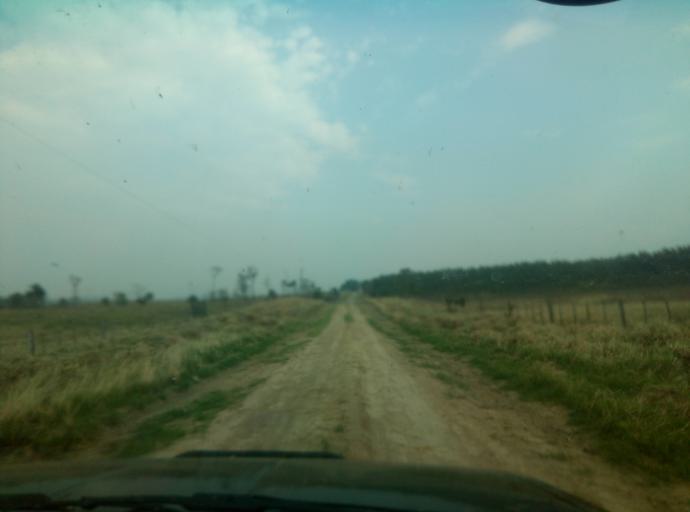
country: PY
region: Caaguazu
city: San Joaquin
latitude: -25.1072
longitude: -56.1276
